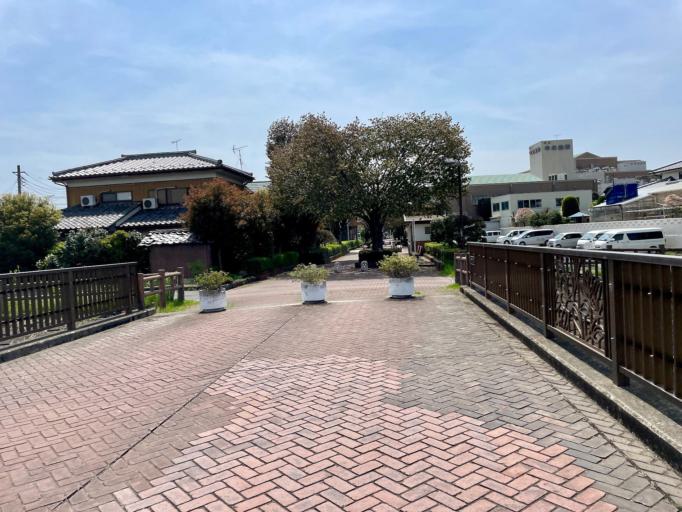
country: JP
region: Saitama
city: Fukayacho
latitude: 36.2052
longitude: 139.2958
